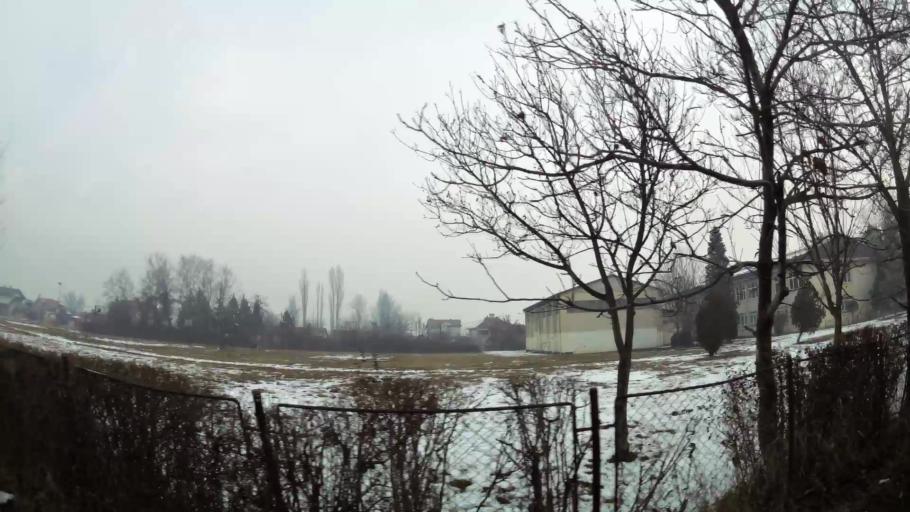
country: MK
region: Ilinden
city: Jurumleri
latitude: 41.9636
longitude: 21.5608
